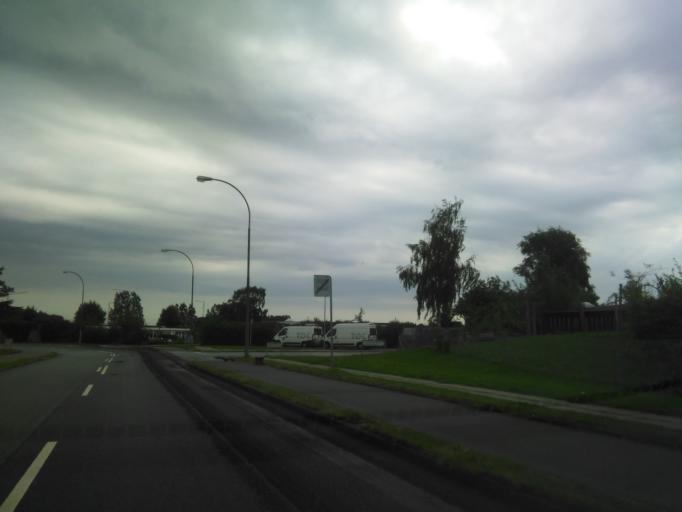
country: DK
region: Central Jutland
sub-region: Arhus Kommune
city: Hjortshoj
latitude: 56.2070
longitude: 10.2710
